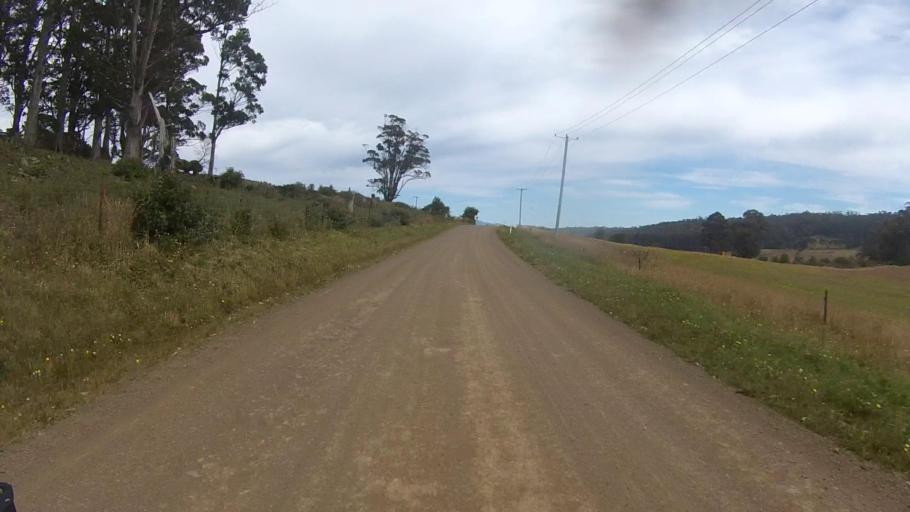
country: AU
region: Tasmania
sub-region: Sorell
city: Sorell
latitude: -42.7219
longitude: 147.7513
